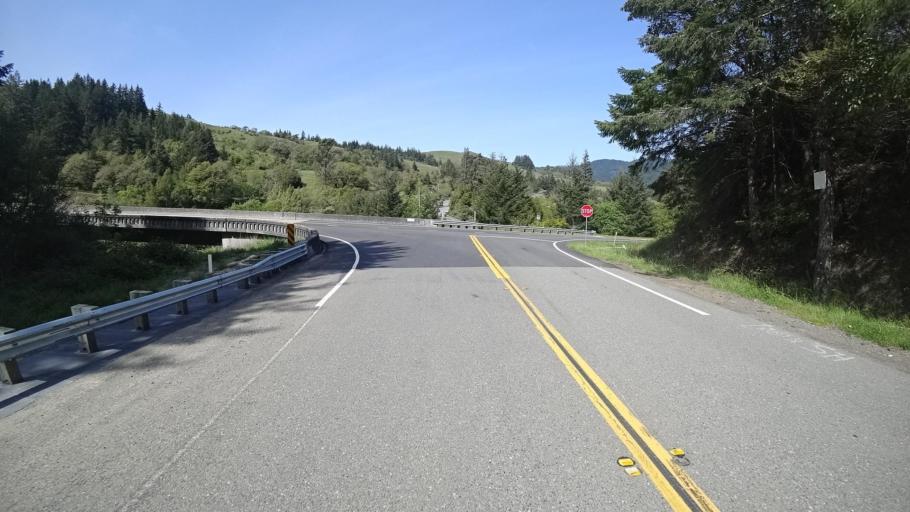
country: US
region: California
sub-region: Humboldt County
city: Hydesville
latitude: 40.4682
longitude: -123.7994
